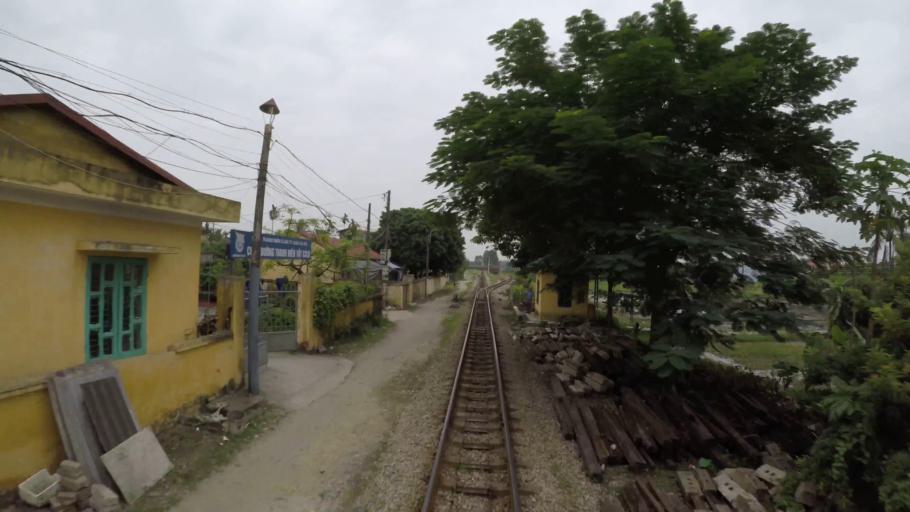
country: VN
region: Hai Phong
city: An Duong
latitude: 20.9080
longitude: 106.5729
